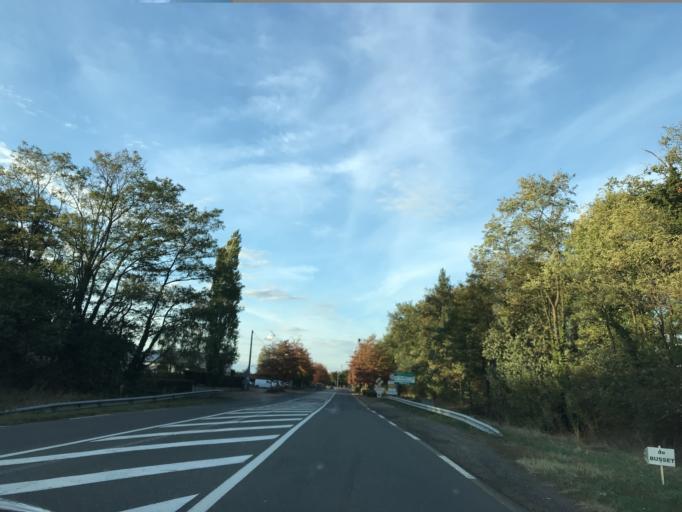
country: FR
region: Auvergne
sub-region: Departement de l'Allier
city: Saint-Yorre
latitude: 46.0505
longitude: 3.4702
